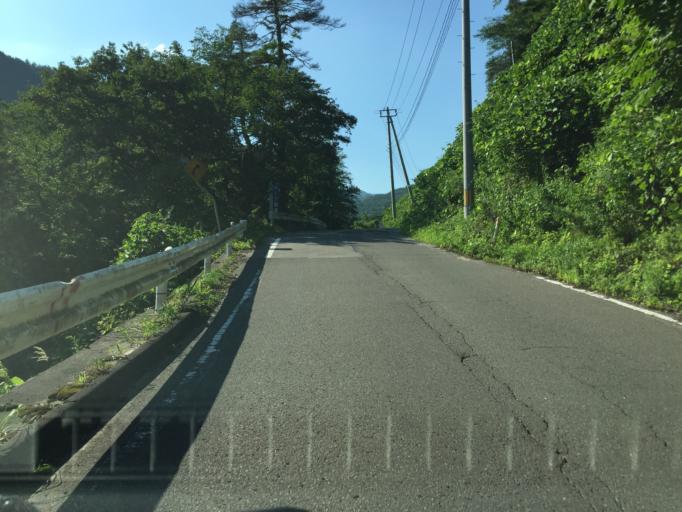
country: JP
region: Fukushima
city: Fukushima-shi
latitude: 37.8678
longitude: 140.4363
